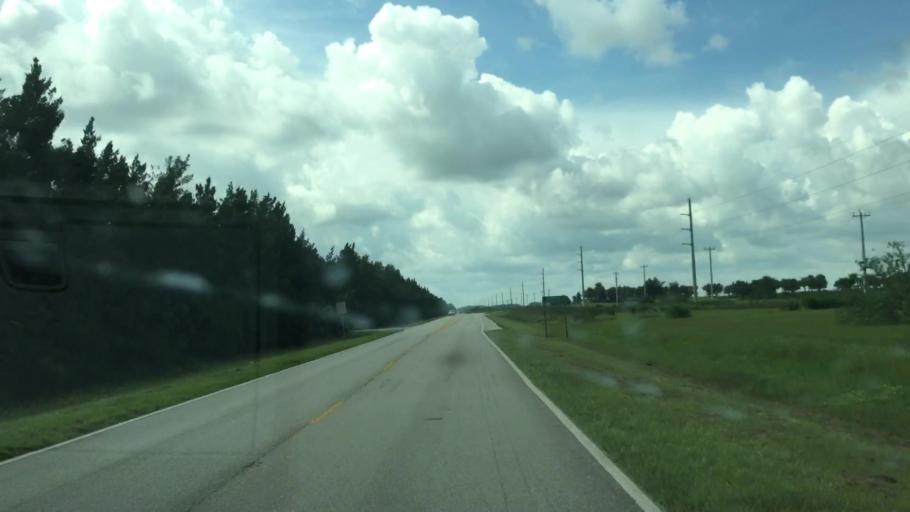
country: US
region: Florida
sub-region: Collier County
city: Immokalee
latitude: 26.3430
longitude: -81.4167
